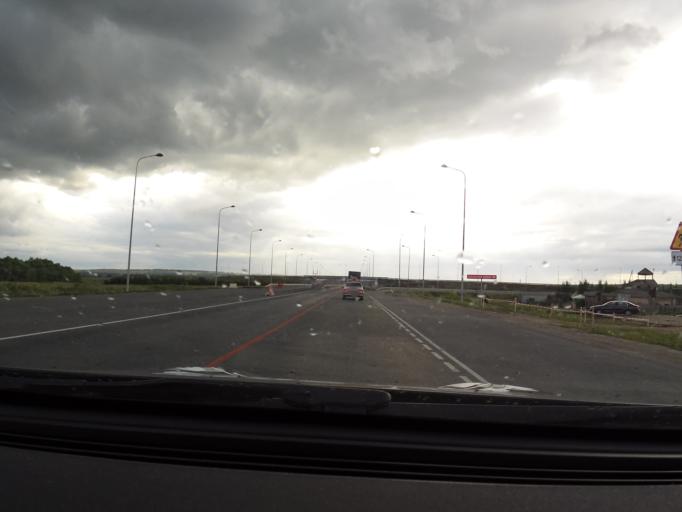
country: RU
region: Tatarstan
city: Nizhniye Vyazovyye
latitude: 55.7233
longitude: 48.5423
